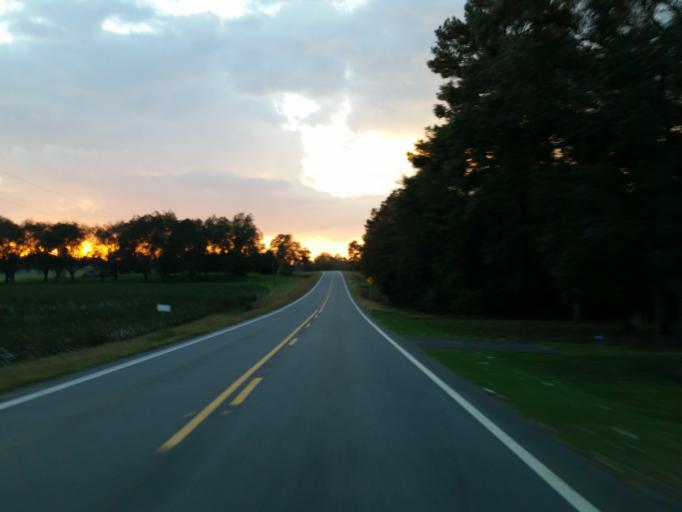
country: US
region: Georgia
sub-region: Pulaski County
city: Hawkinsville
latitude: 32.2082
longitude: -83.5599
